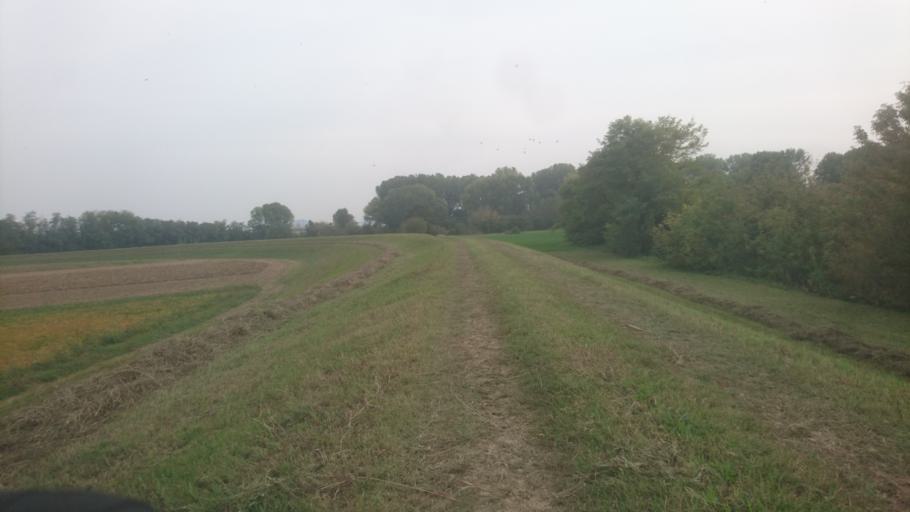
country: IT
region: Veneto
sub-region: Provincia di Padova
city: Cervarese Santa Croce
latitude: 45.4185
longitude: 11.7102
